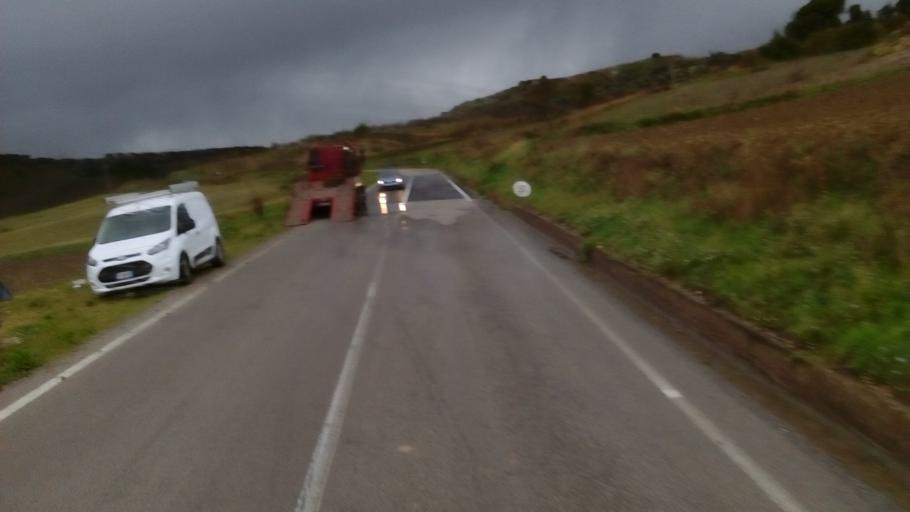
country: IT
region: Sicily
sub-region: Enna
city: Pietraperzia
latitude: 37.4442
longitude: 14.1777
